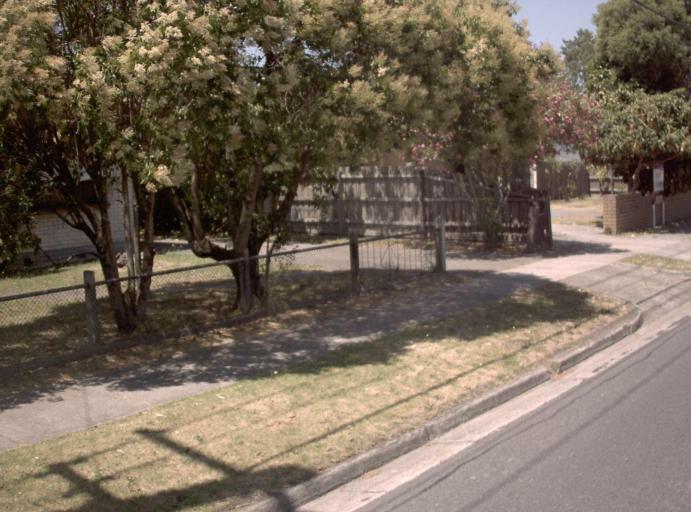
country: AU
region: Victoria
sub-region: Whitehorse
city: Nunawading
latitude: -37.8165
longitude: 145.1764
